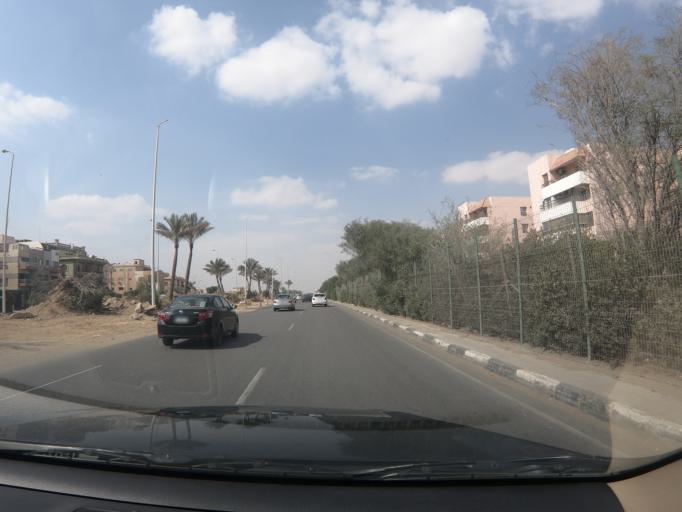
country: EG
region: Muhafazat al Qalyubiyah
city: Al Khankah
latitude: 30.0616
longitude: 31.4752
